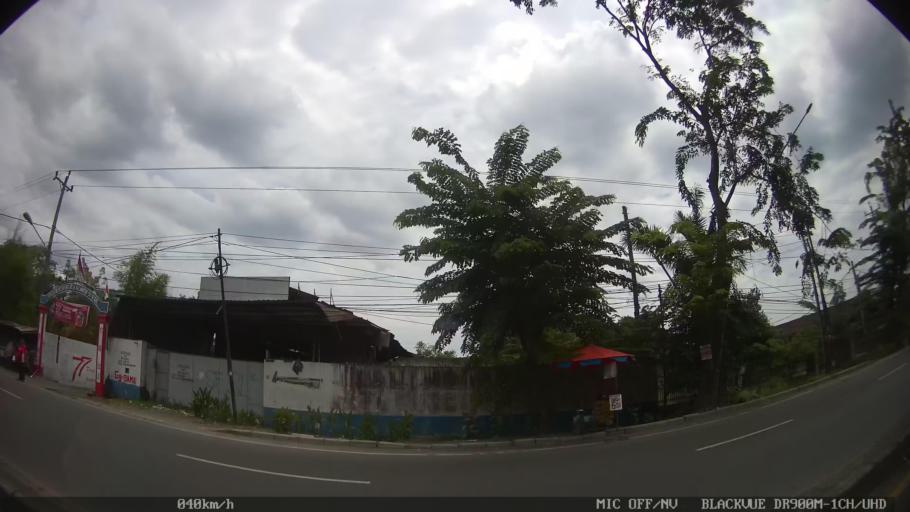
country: ID
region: North Sumatra
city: Sunggal
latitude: 3.5990
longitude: 98.5991
